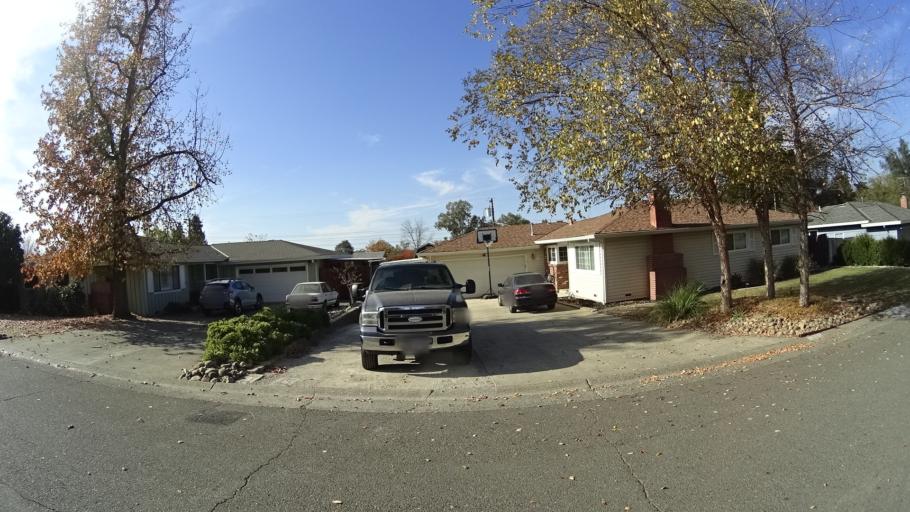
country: US
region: California
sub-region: Sacramento County
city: Fair Oaks
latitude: 38.6700
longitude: -121.2870
